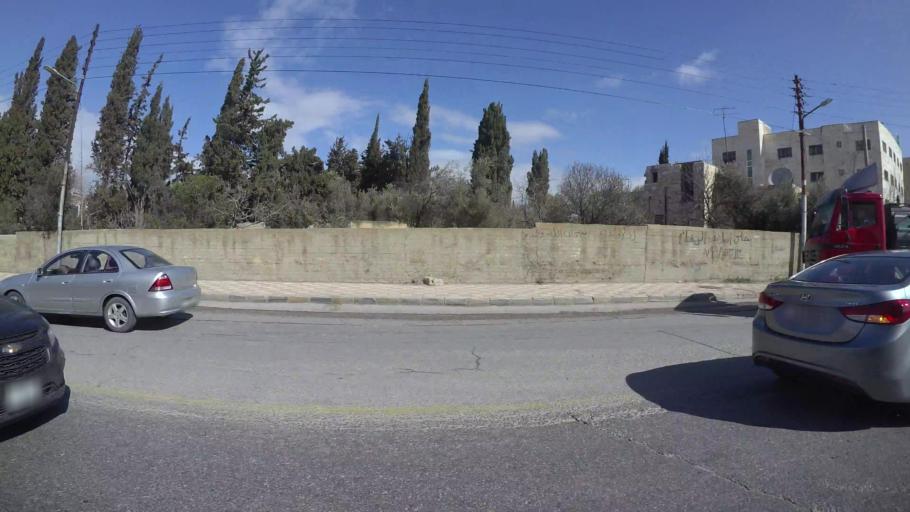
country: JO
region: Amman
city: Al Jubayhah
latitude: 32.0162
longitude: 35.8449
